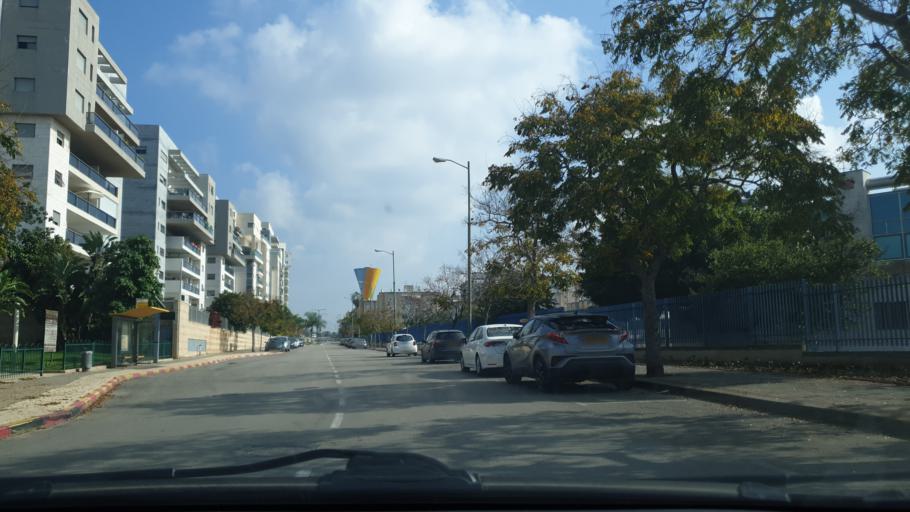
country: IL
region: Central District
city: Bet Dagan
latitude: 31.9687
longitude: 34.8210
